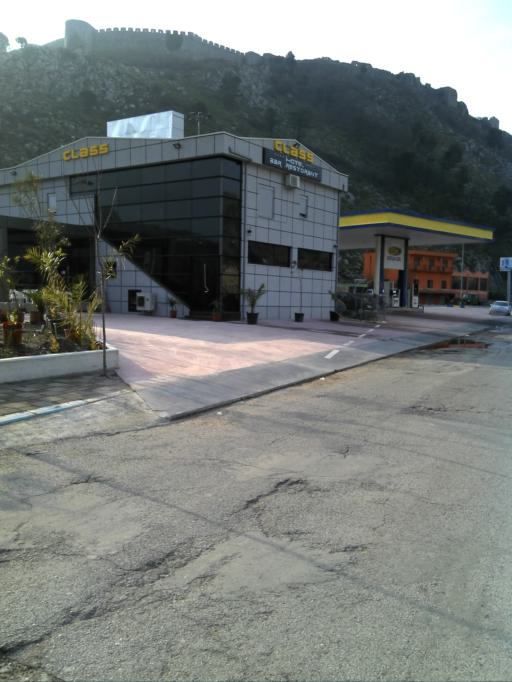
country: AL
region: Shkoder
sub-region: Rrethi i Shkodres
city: Shkoder
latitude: 42.0494
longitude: 19.4923
